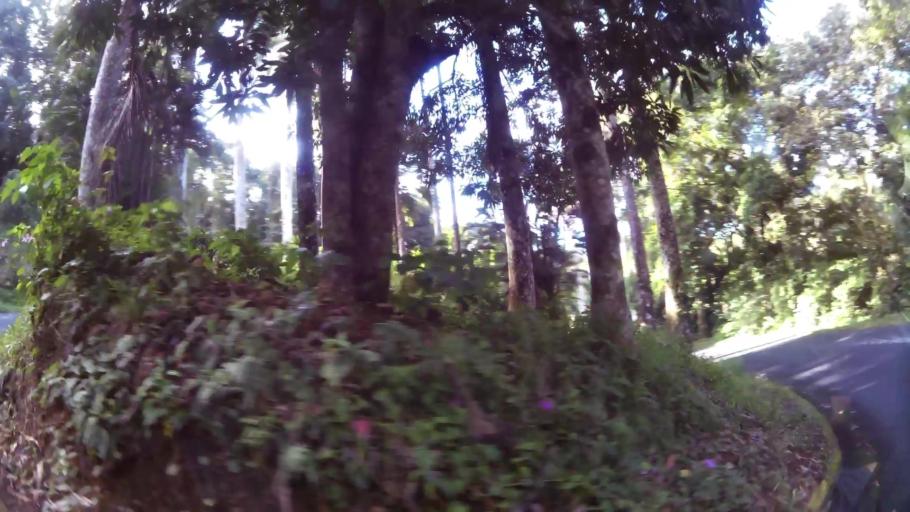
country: DM
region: Saint John
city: Portsmouth
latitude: 15.5780
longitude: -61.4252
